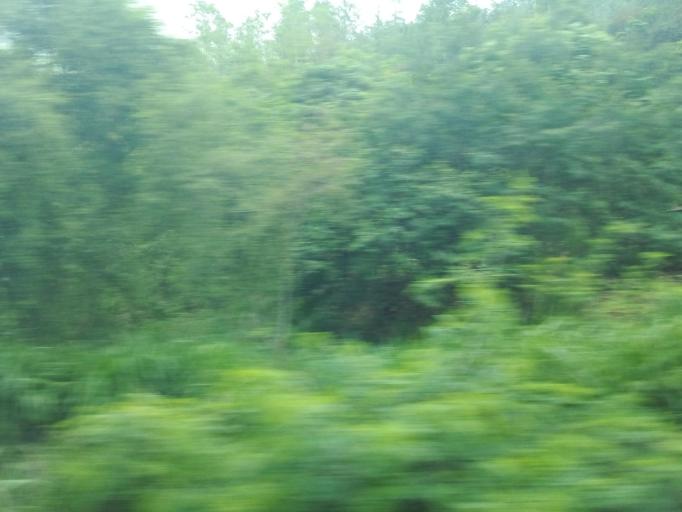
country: BR
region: Minas Gerais
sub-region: Rio Piracicaba
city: Rio Piracicaba
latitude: -19.8944
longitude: -43.1426
